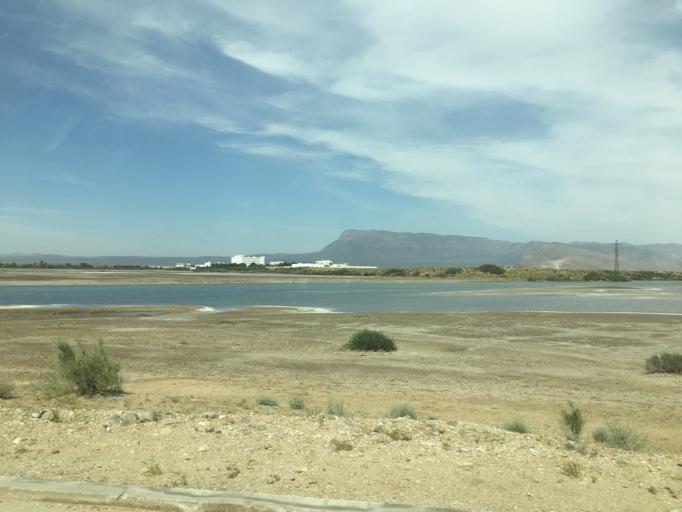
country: TM
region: Balkan
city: Balkanabat
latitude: 39.6206
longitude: 54.1628
